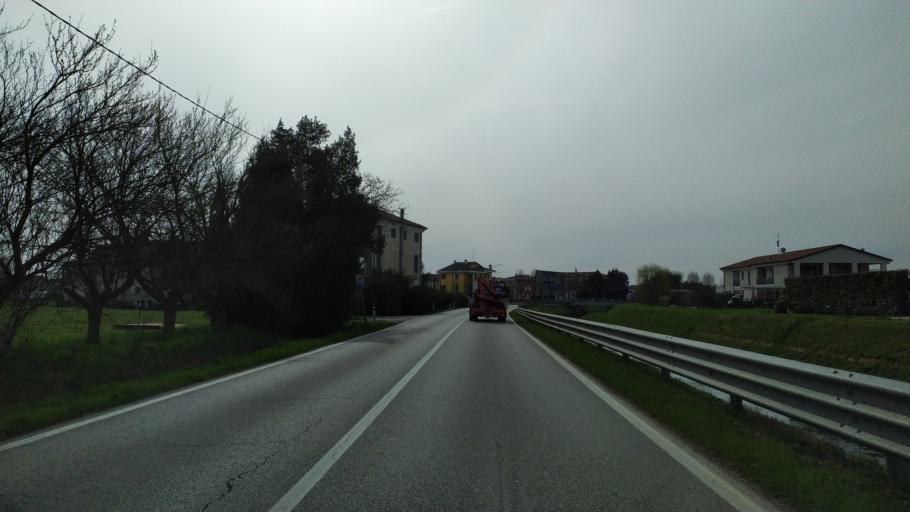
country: IT
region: Veneto
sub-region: Provincia di Padova
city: San Giorgio delle Pertiche
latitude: 45.5455
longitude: 11.8749
